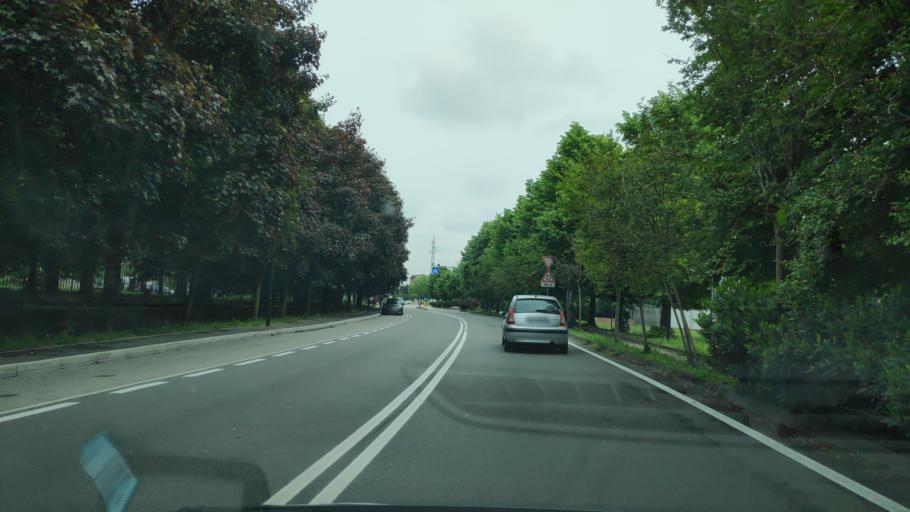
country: IT
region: Lombardy
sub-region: Citta metropolitana di Milano
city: Segrate
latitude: 45.4927
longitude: 9.2995
